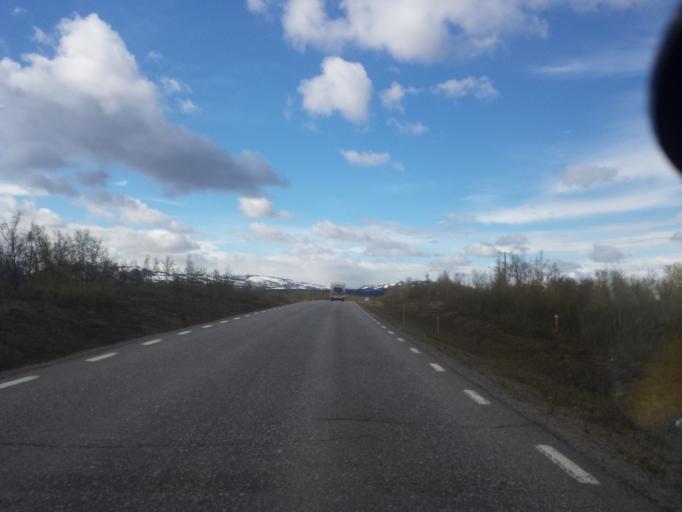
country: SE
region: Norrbotten
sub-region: Kiruna Kommun
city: Kiruna
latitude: 68.0021
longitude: 19.8576
